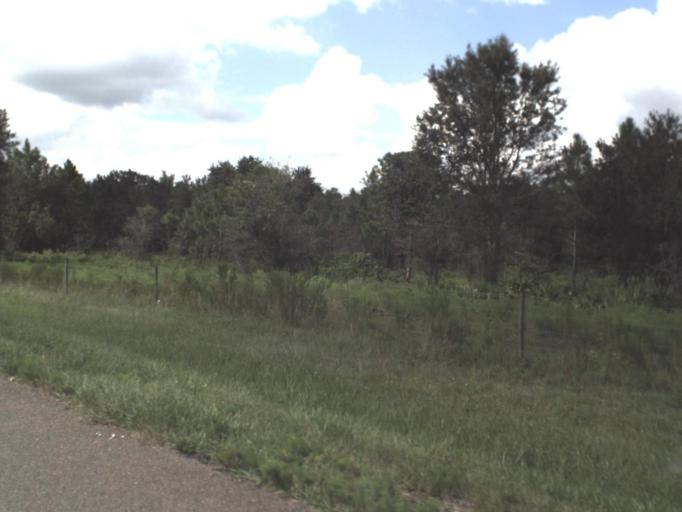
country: US
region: Florida
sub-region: Hardee County
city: Wauchula
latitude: 27.4852
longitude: -81.9397
